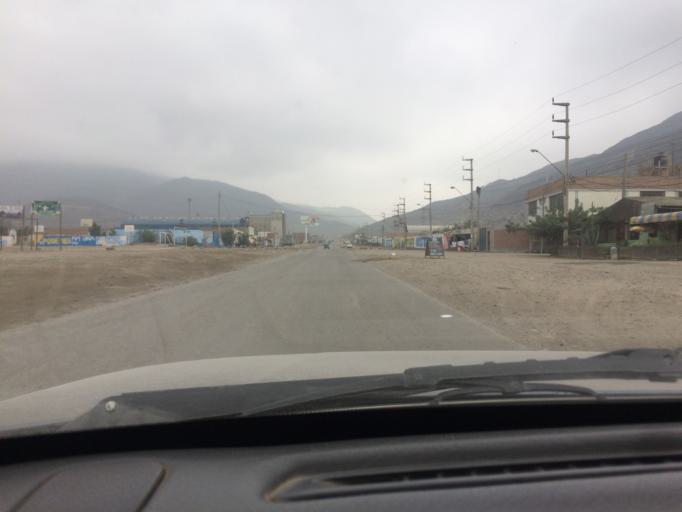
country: PE
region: Lima
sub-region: Lima
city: Cieneguilla
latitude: -12.1607
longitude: -76.8672
